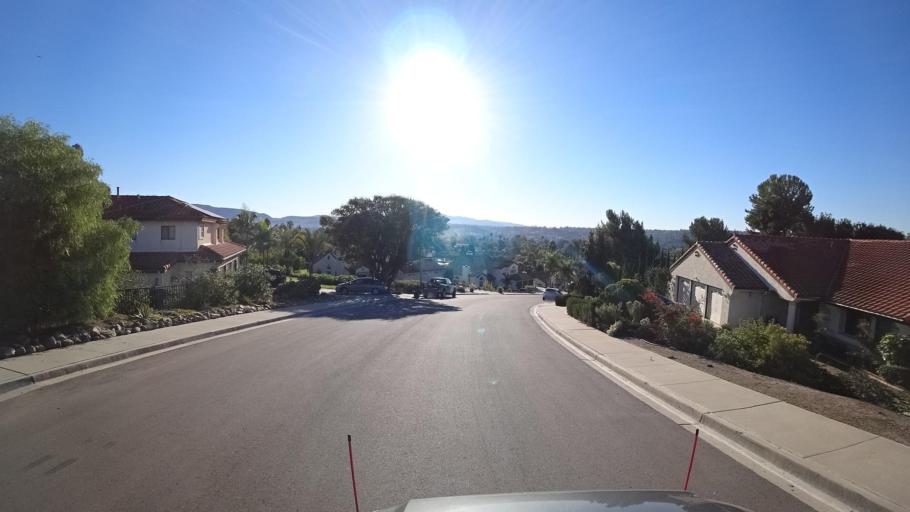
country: US
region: California
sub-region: San Diego County
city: Bonita
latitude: 32.6752
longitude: -117.0327
